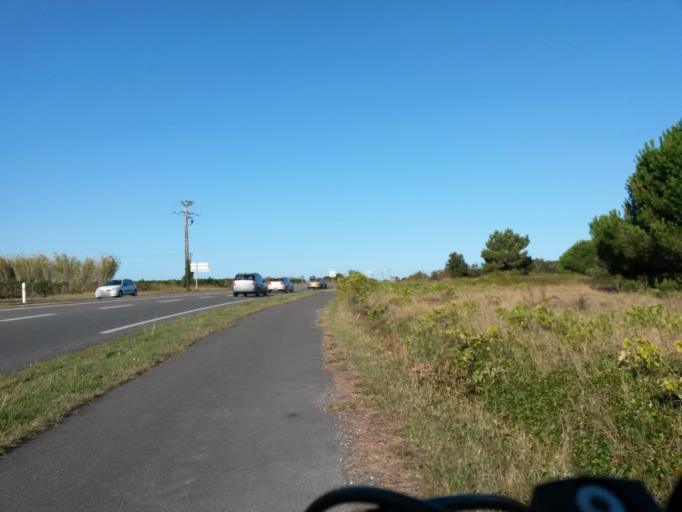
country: FR
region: Poitou-Charentes
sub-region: Departement de la Charente-Maritime
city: Sainte-Marie-de-Re
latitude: 46.1538
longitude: -1.2938
